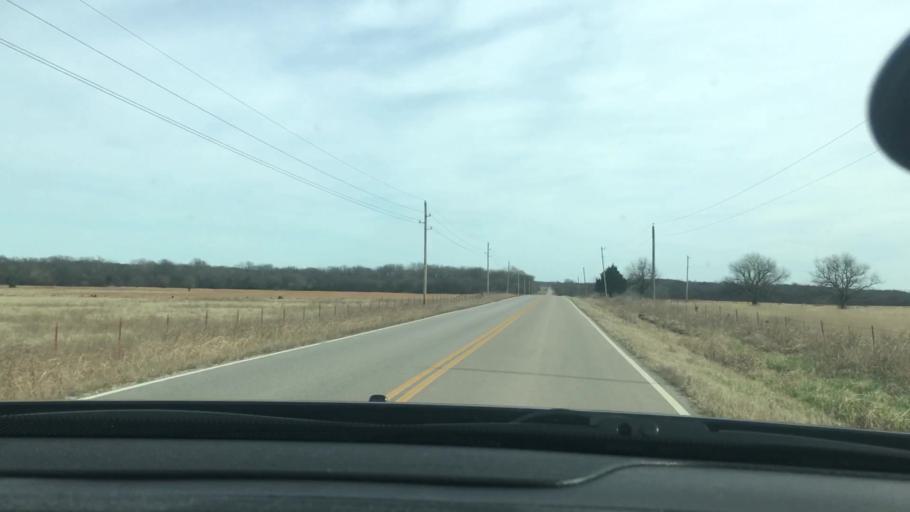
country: US
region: Oklahoma
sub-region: Murray County
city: Sulphur
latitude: 34.4049
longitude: -96.8738
